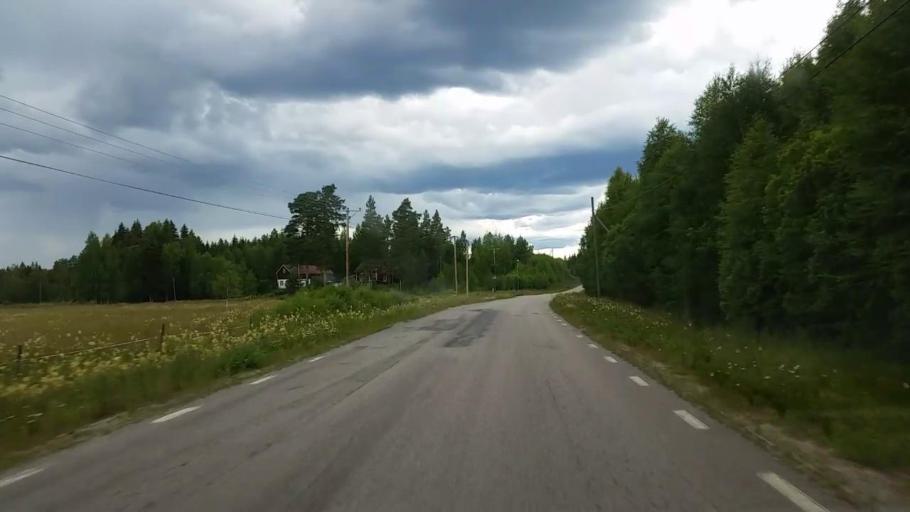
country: SE
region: Gaevleborg
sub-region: Ovanakers Kommun
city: Edsbyn
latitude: 61.4569
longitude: 15.8763
